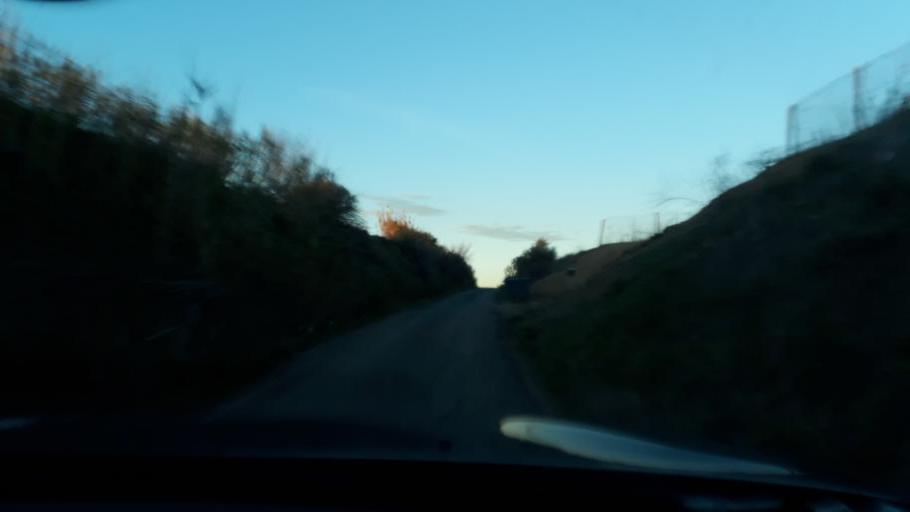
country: FR
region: Languedoc-Roussillon
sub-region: Departement de l'Herault
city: Florensac
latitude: 43.3976
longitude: 3.4593
